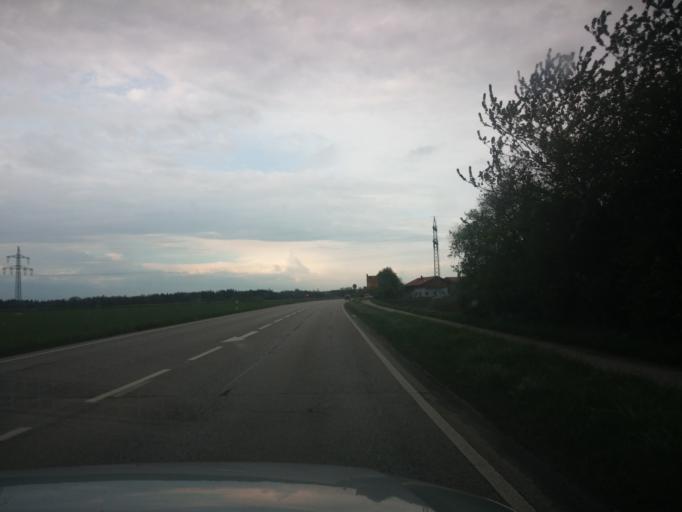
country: DE
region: Bavaria
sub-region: Upper Bavaria
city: Putzbrunn
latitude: 48.0802
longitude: 11.7167
